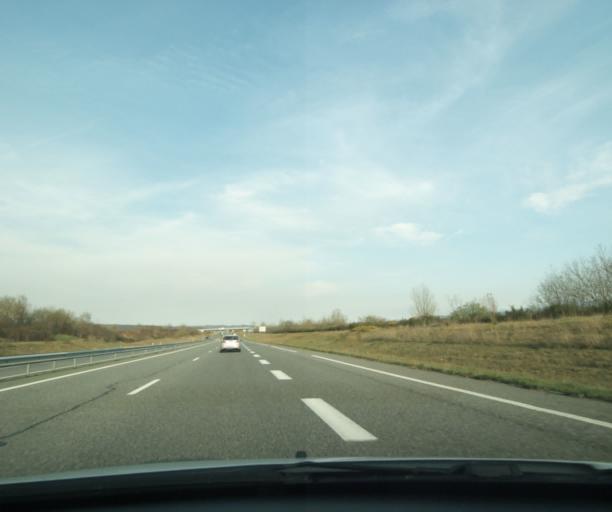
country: FR
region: Midi-Pyrenees
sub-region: Departement de la Haute-Garonne
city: Montrejeau
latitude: 43.1045
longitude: 0.5982
